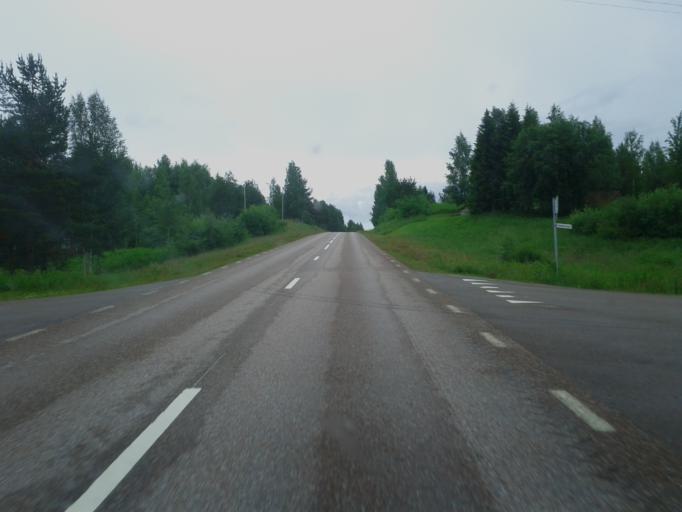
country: NO
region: Hedmark
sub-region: Trysil
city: Innbygda
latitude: 61.7338
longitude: 12.9837
